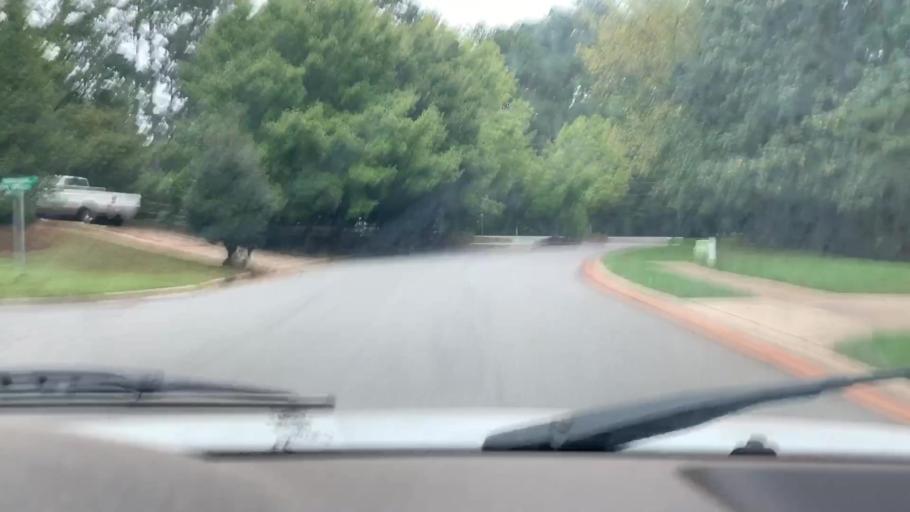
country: US
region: North Carolina
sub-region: Catawba County
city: Lake Norman of Catawba
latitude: 35.5494
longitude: -80.9075
